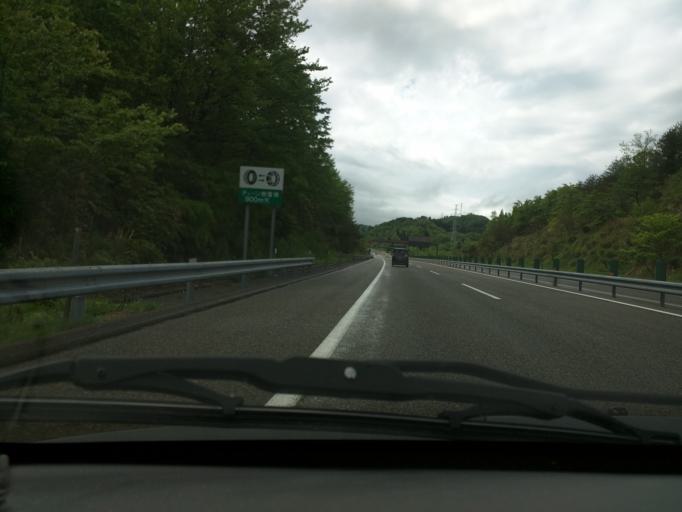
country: JP
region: Niigata
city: Joetsu
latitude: 37.1345
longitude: 138.2133
